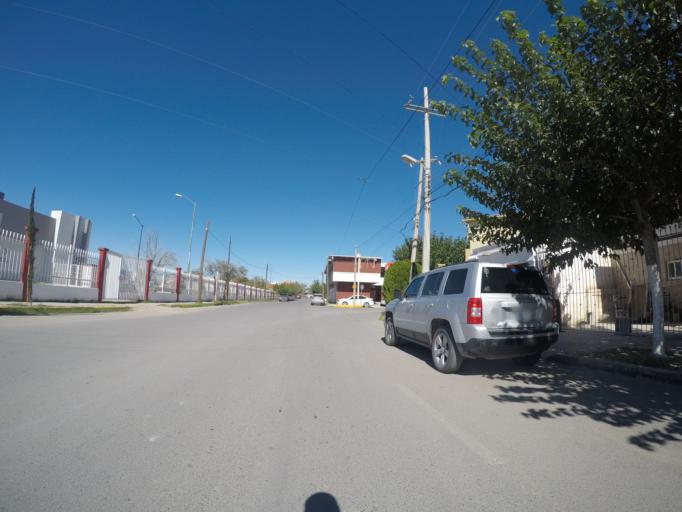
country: MX
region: Chihuahua
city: Ciudad Juarez
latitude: 31.7188
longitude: -106.4189
